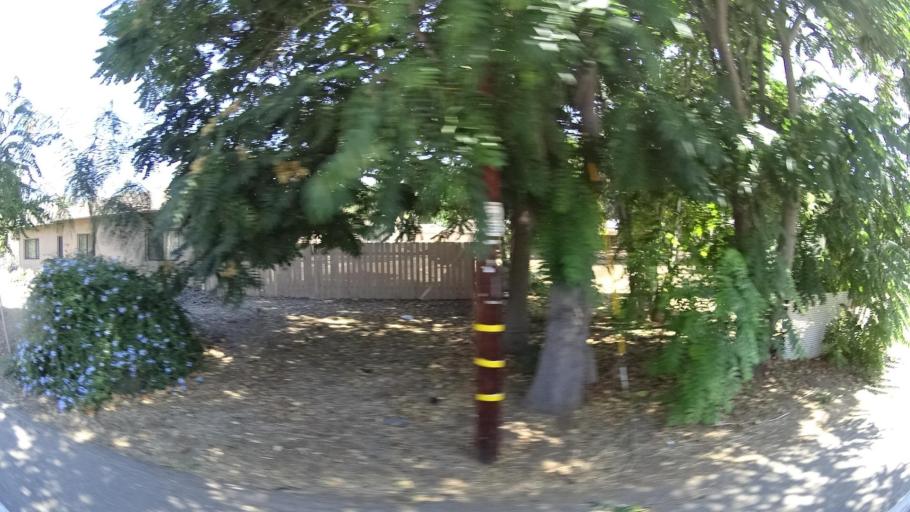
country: US
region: California
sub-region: San Diego County
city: Granite Hills
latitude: 32.8076
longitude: -116.9111
